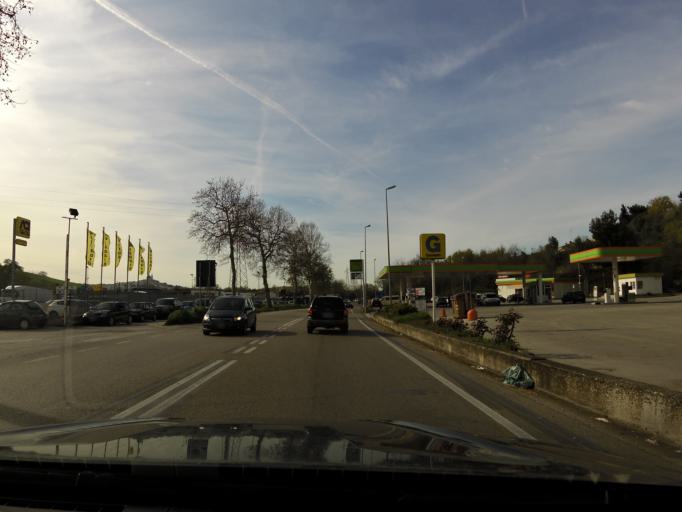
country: IT
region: The Marches
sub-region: Provincia di Macerata
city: Porto Recanati
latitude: 43.4363
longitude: 13.6443
